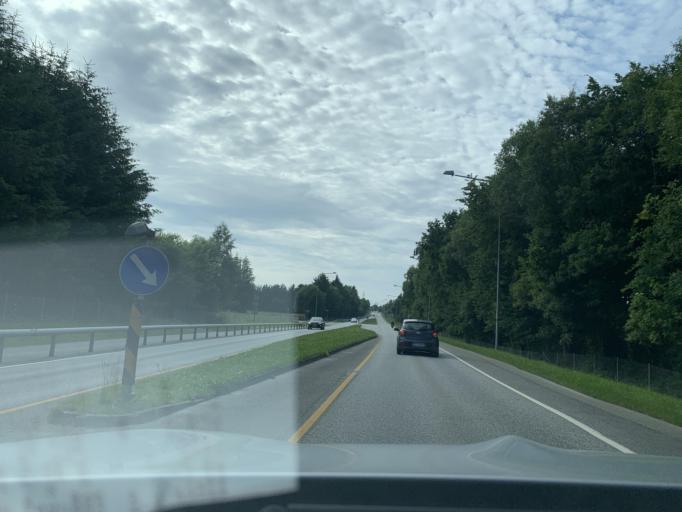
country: NO
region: Rogaland
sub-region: Stavanger
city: Stavanger
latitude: 58.9164
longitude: 5.7199
